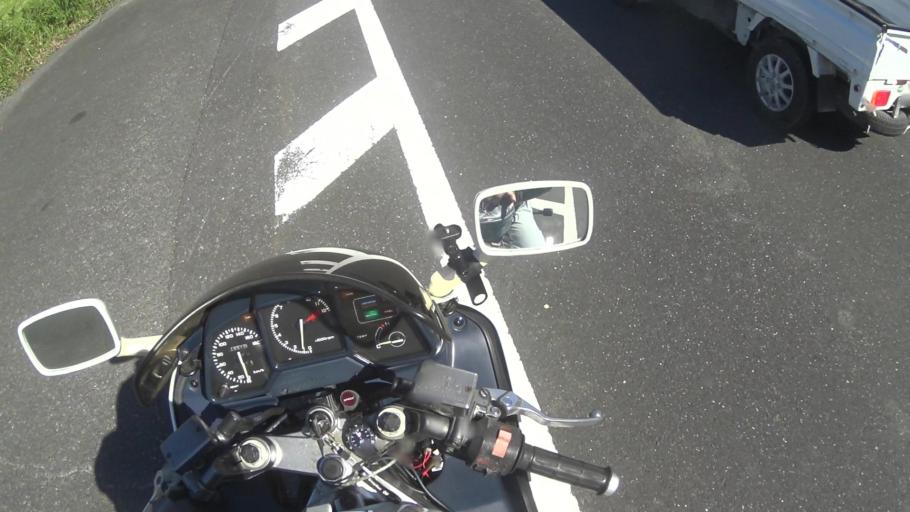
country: JP
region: Hyogo
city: Toyooka
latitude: 35.5862
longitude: 134.9487
